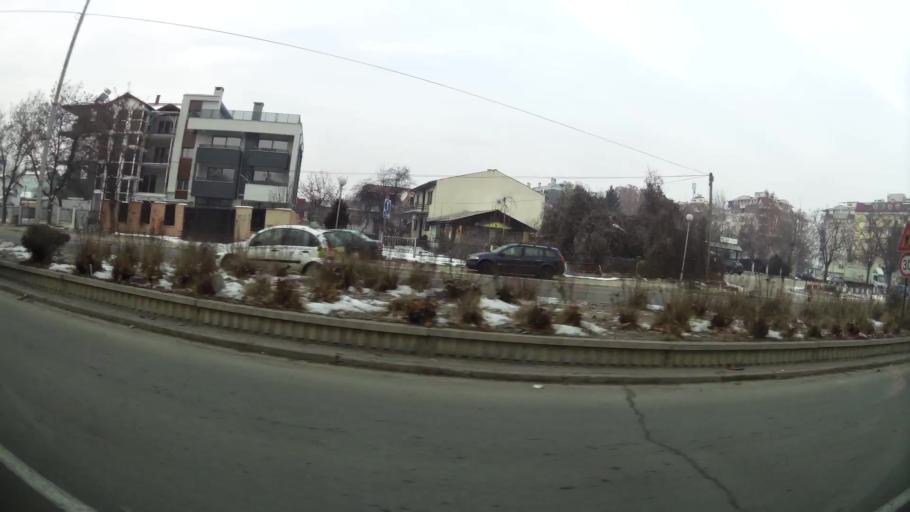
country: MK
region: Butel
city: Butel
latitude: 42.0239
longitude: 21.4502
